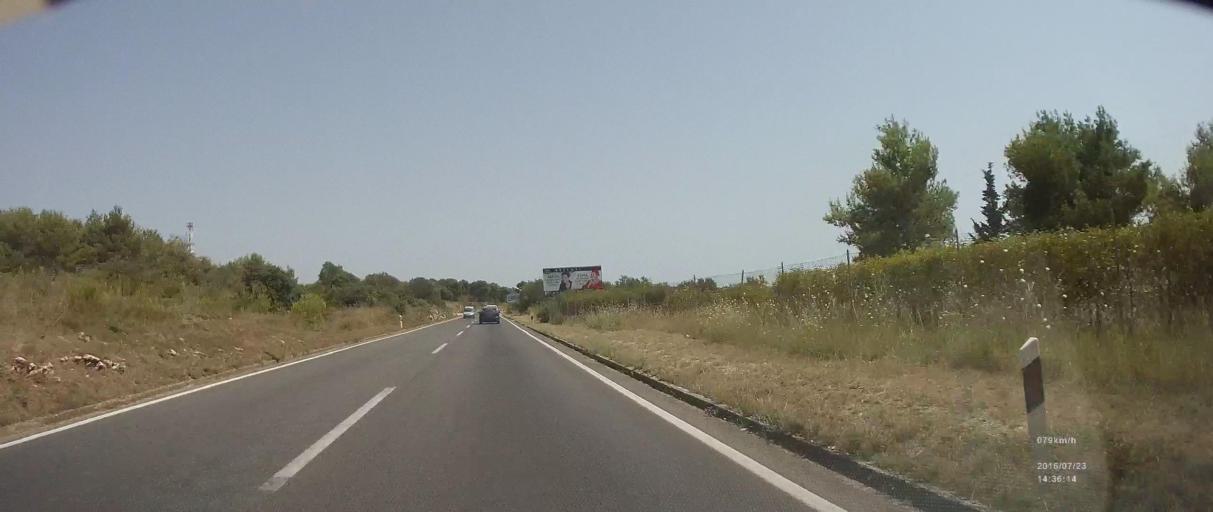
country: HR
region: Zadarska
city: Biograd na Moru
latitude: 43.9534
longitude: 15.4434
